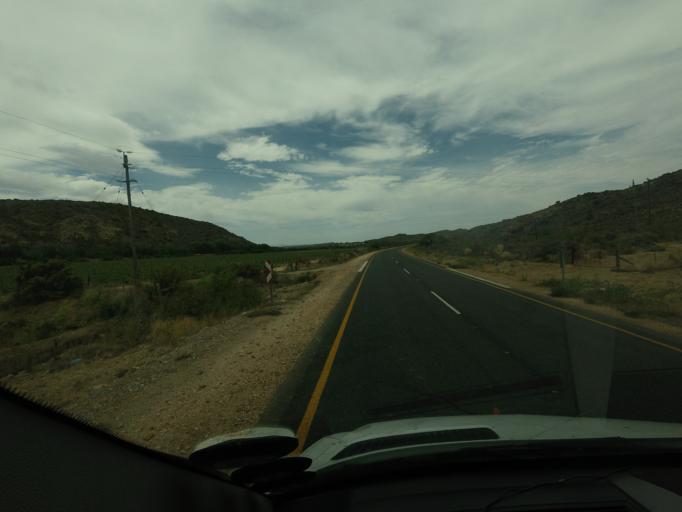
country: ZA
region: Western Cape
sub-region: Overberg District Municipality
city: Swellendam
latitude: -33.8504
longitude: 20.8370
